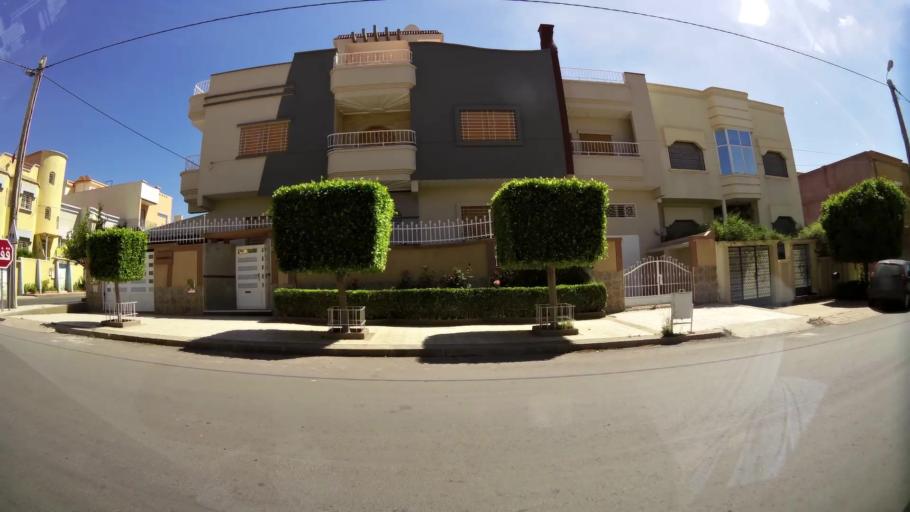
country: MA
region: Oriental
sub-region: Oujda-Angad
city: Oujda
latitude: 34.6490
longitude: -1.9036
